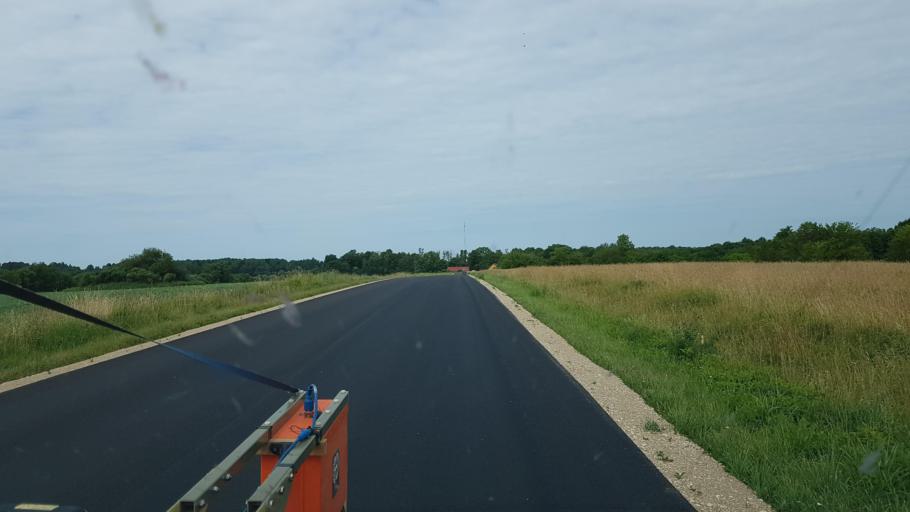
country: EE
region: Paernumaa
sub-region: Halinga vald
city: Parnu-Jaagupi
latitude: 58.6222
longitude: 24.3862
